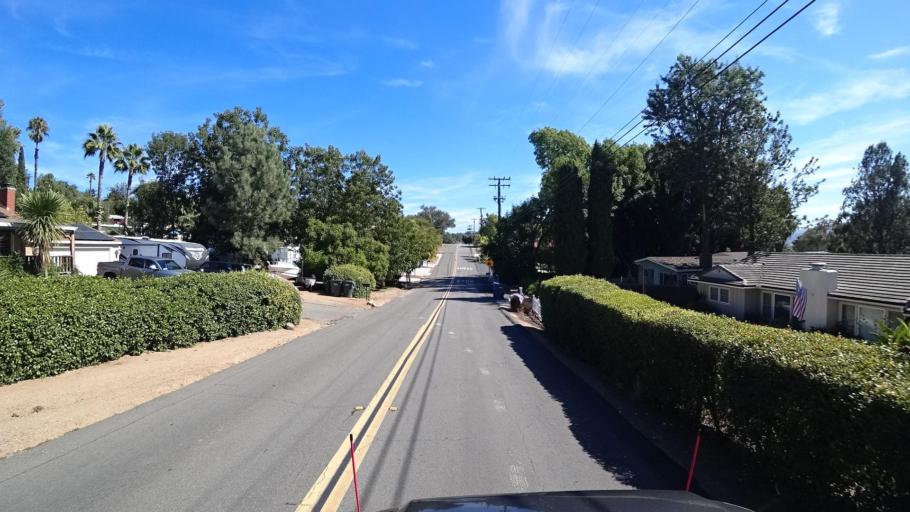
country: US
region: California
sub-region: San Diego County
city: Casa de Oro-Mount Helix
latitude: 32.7555
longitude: -116.9670
